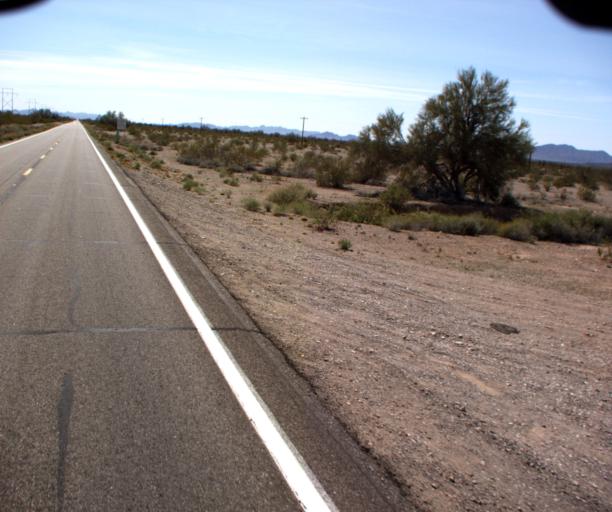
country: US
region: Arizona
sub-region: La Paz County
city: Quartzsite
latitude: 33.5295
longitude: -114.2170
